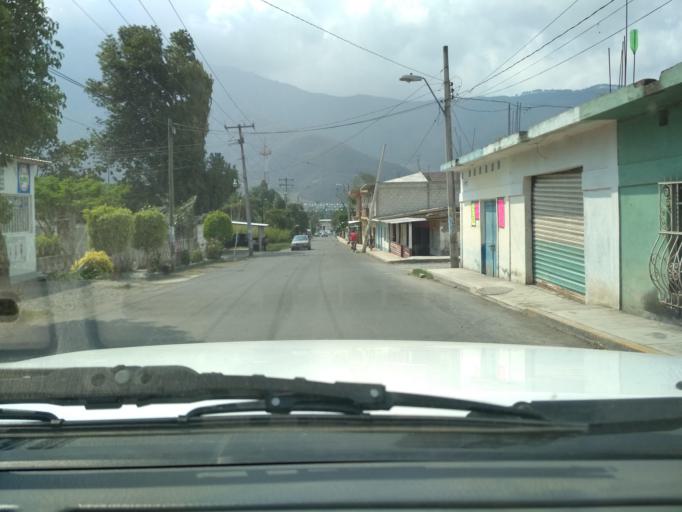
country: MX
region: Veracruz
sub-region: Acultzingo
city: Acatla
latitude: 18.7586
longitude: -97.2256
